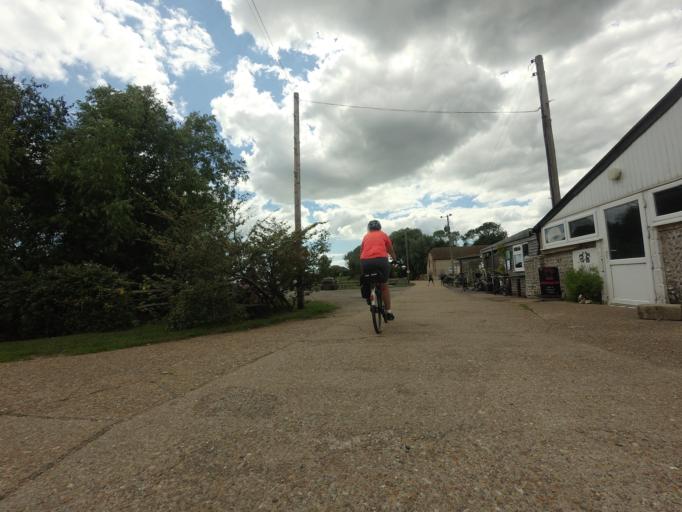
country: GB
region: England
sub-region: East Sussex
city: Pevensey
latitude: 50.8320
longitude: 0.3254
